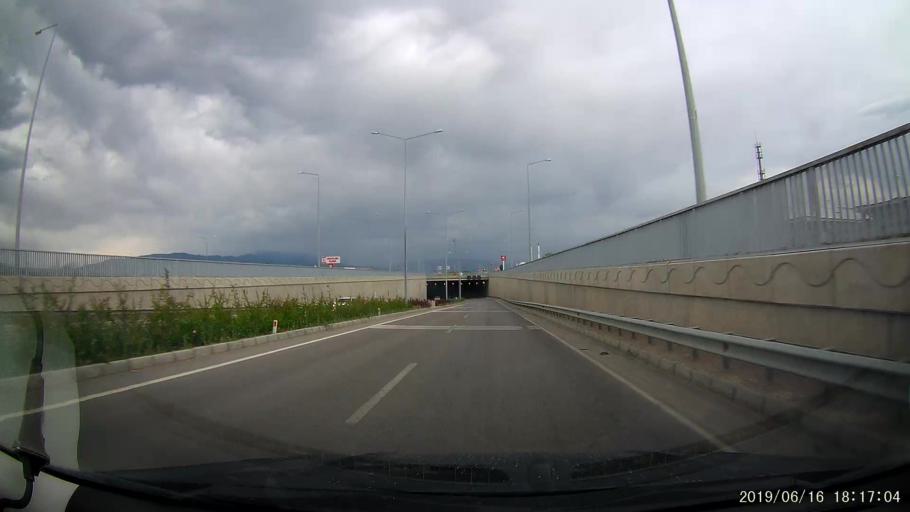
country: TR
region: Erzincan
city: Erzincan
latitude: 39.7322
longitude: 39.5383
